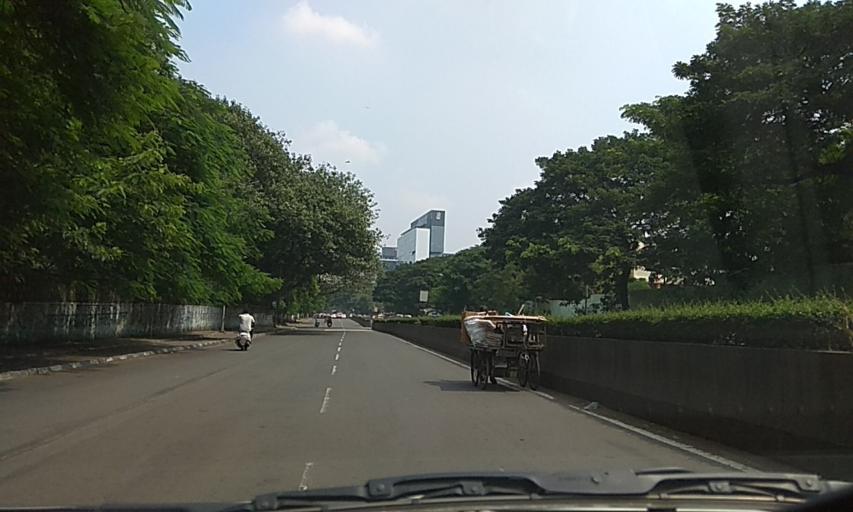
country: IN
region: Maharashtra
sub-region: Pune Division
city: Khadki
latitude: 18.5532
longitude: 73.8857
